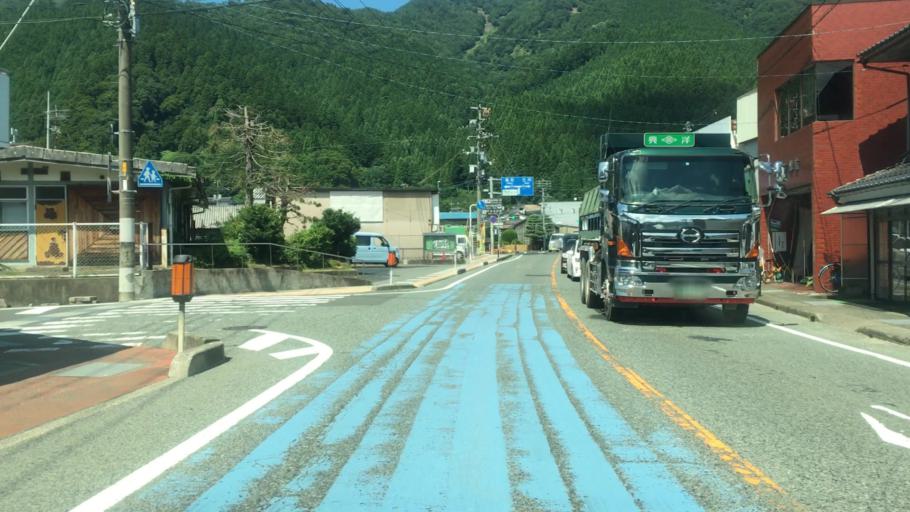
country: JP
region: Tottori
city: Tottori
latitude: 35.2669
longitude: 134.2291
